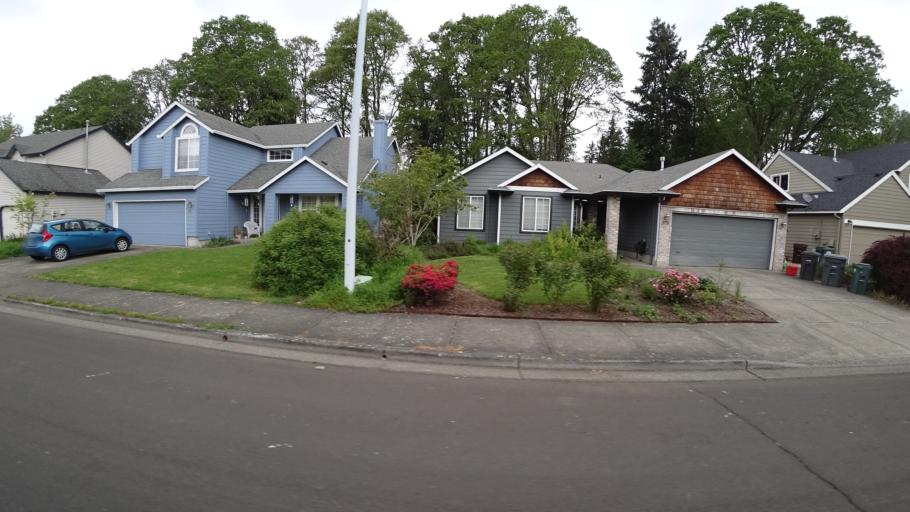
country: US
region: Oregon
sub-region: Washington County
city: Hillsboro
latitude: 45.5428
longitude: -122.9766
